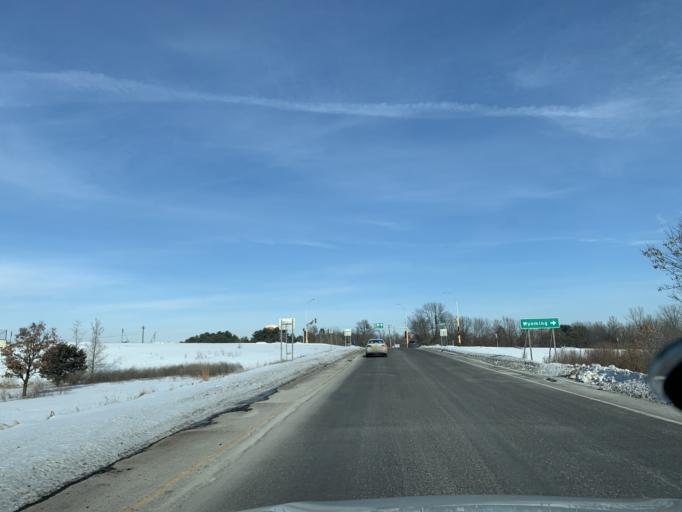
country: US
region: Minnesota
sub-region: Chisago County
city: Wyoming
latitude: 45.3354
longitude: -93.0039
